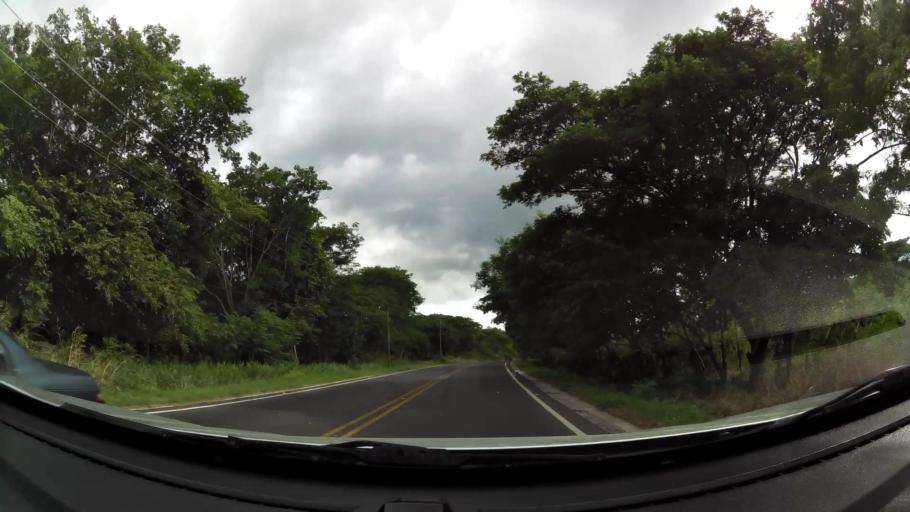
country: CR
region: Guanacaste
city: Nandayure
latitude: 10.2428
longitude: -85.2221
